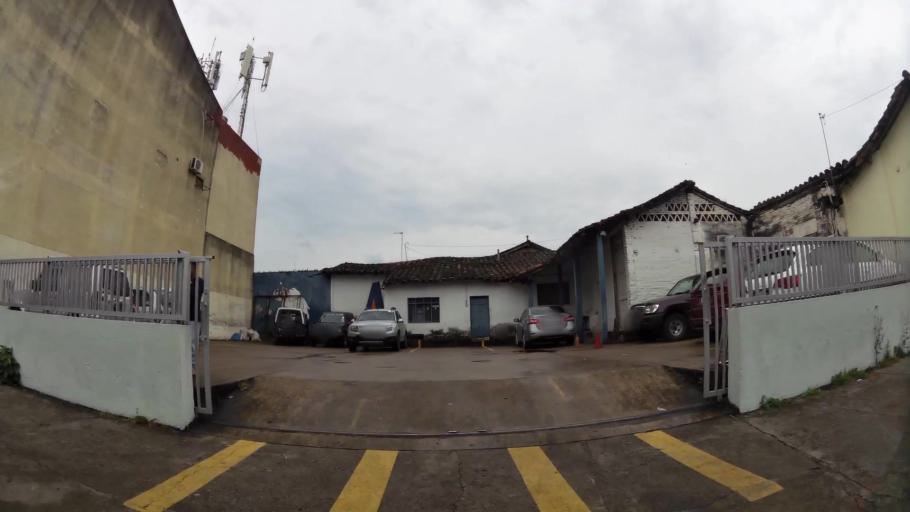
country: BO
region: Santa Cruz
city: Santa Cruz de la Sierra
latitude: -17.7852
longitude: -63.1814
